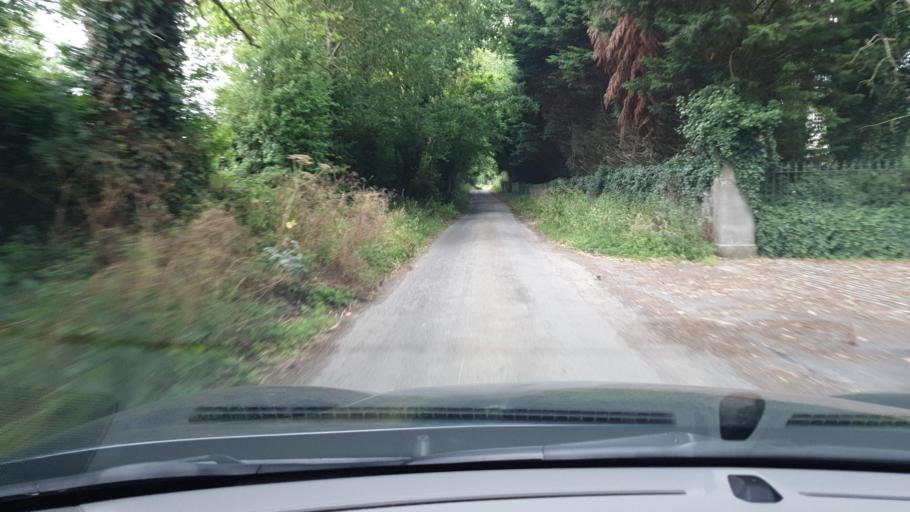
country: IE
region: Leinster
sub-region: An Mhi
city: Ashbourne
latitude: 53.5380
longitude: -6.3888
